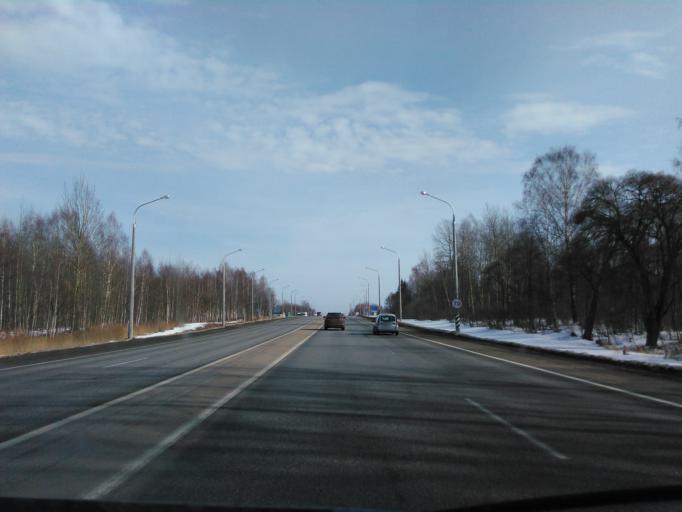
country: RU
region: Smolensk
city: Rudnya
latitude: 54.6903
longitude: 30.9623
